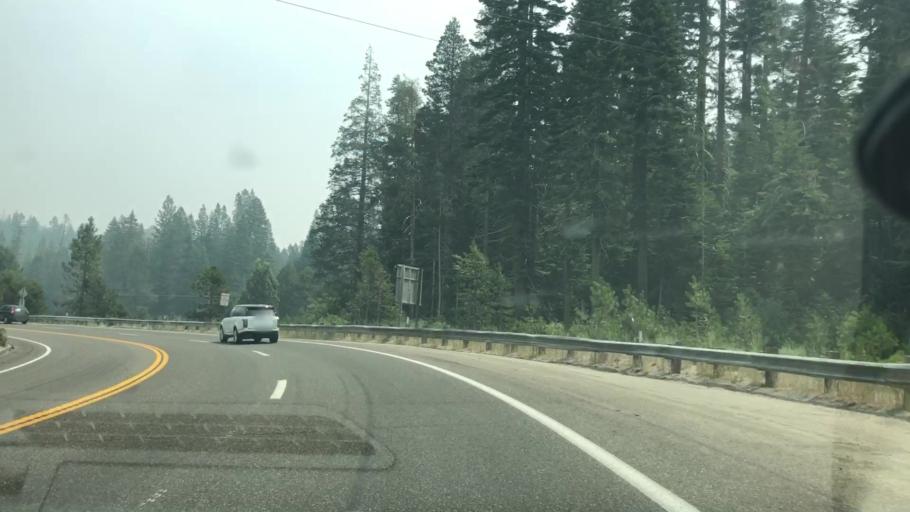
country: US
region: California
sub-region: El Dorado County
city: South Lake Tahoe
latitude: 38.8016
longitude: -120.1203
